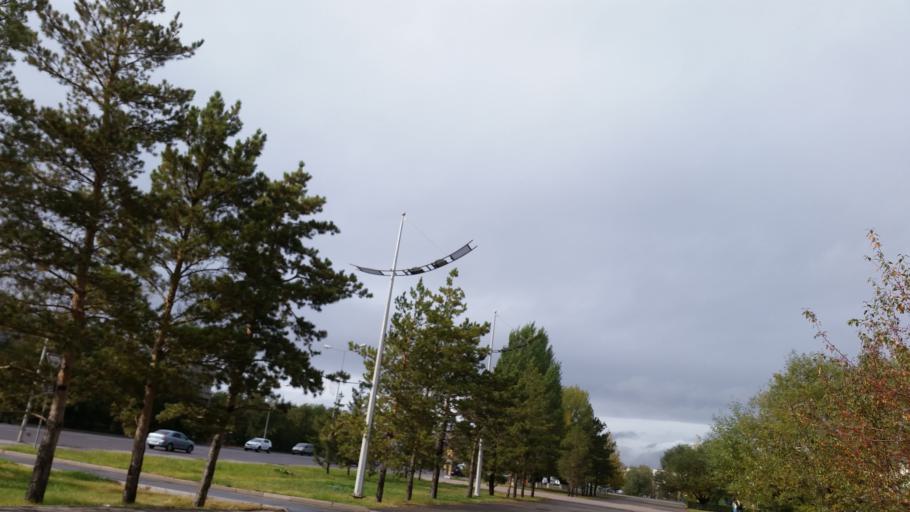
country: KZ
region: Astana Qalasy
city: Astana
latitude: 51.1527
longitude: 71.4560
